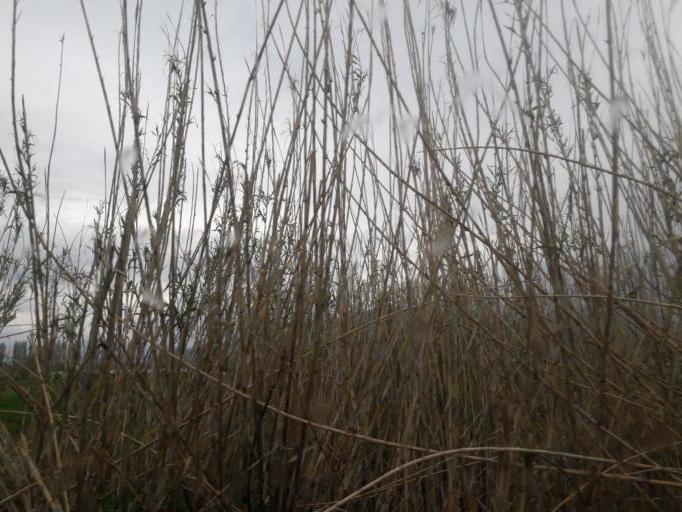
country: AL
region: Shkoder
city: Vukatane
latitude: 42.0003
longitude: 19.5425
